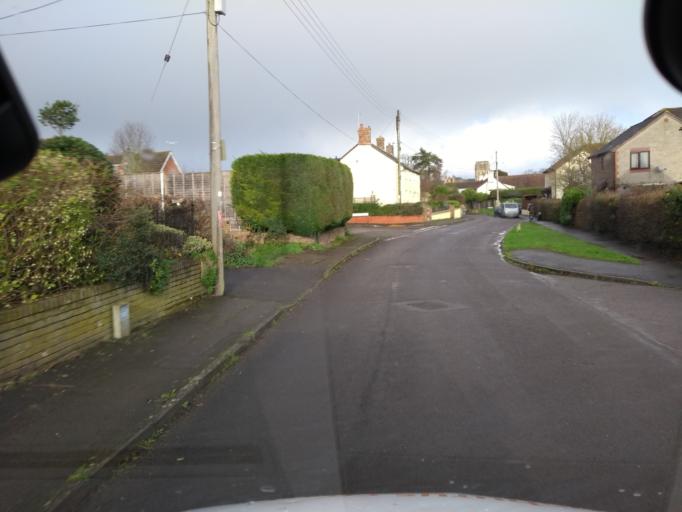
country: GB
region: England
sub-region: Somerset
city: Creech Saint Michael
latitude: 51.0184
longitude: -3.0506
